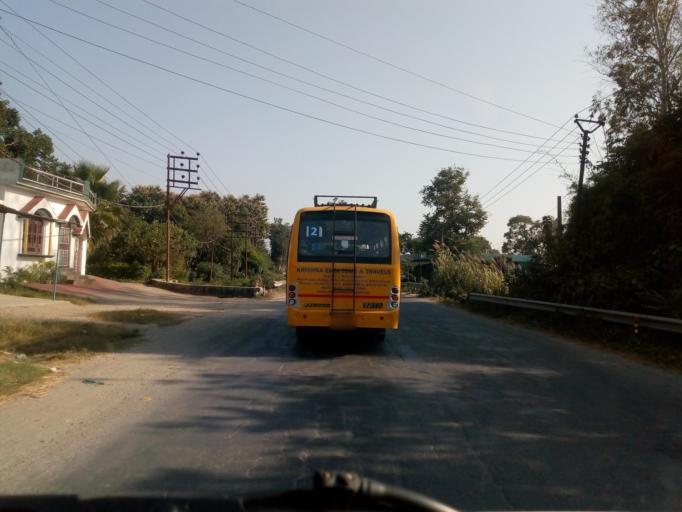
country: IN
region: Uttarakhand
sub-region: Dehradun
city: Harbatpur
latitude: 30.4027
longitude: 77.7964
